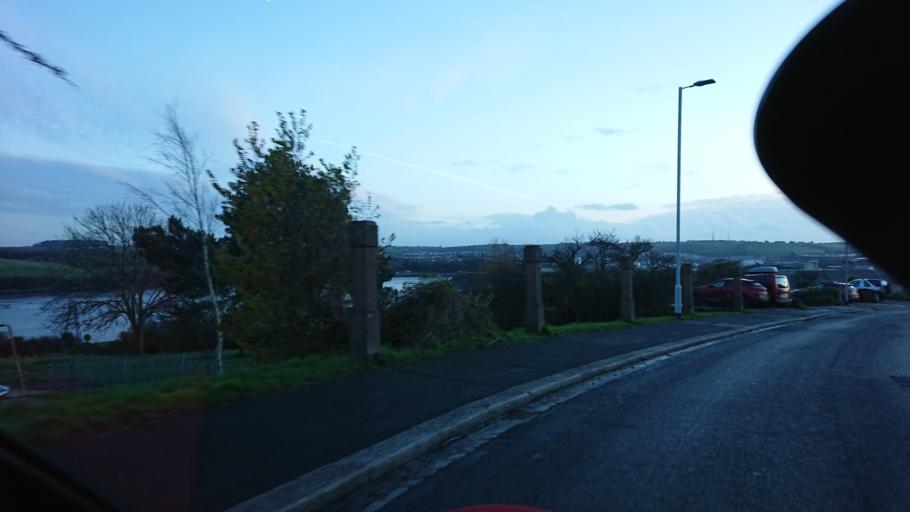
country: GB
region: England
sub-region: Plymouth
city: Plymstock
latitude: 50.3790
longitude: -4.1090
